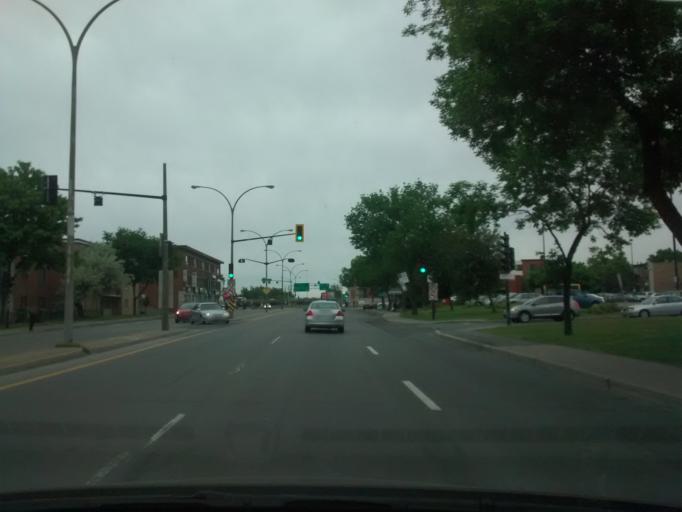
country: CA
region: Quebec
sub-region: Montreal
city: Saint-Leonard
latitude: 45.5723
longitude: -73.6046
